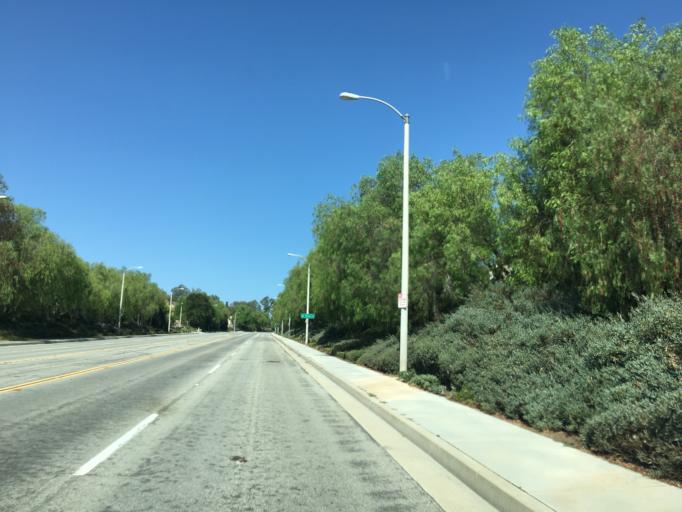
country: US
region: California
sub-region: Los Angeles County
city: Castaic
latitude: 34.4710
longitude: -118.6221
